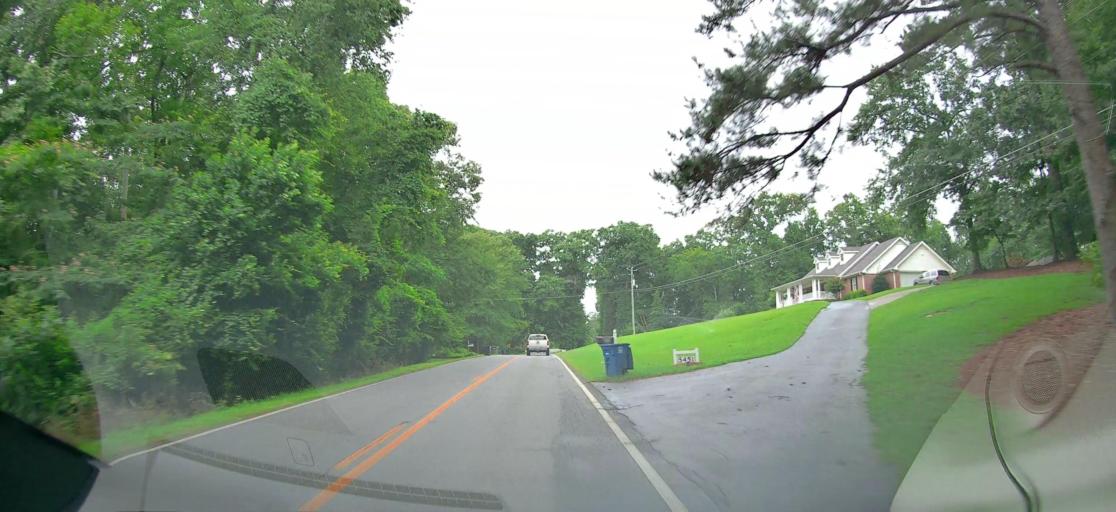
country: US
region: Georgia
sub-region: Peach County
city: Byron
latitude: 32.7169
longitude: -83.7409
